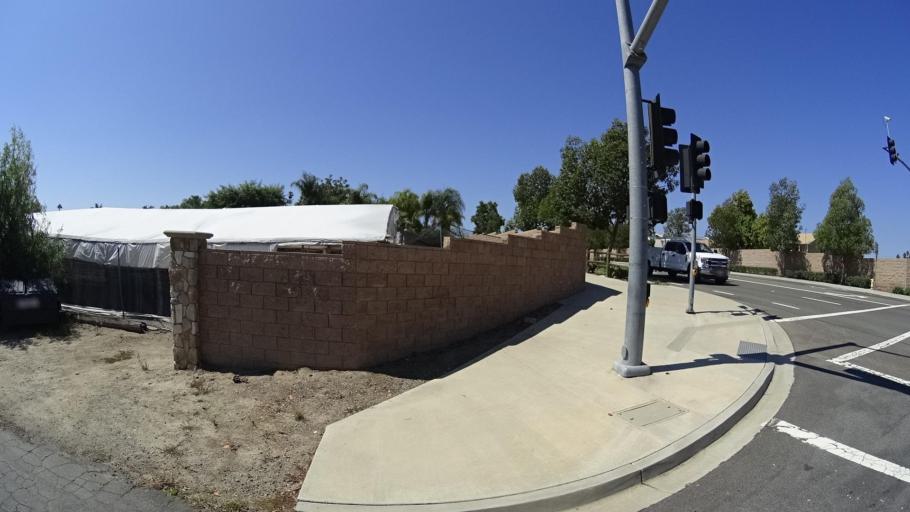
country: US
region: California
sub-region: San Diego County
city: Lake San Marcos
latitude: 33.1425
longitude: -117.2098
